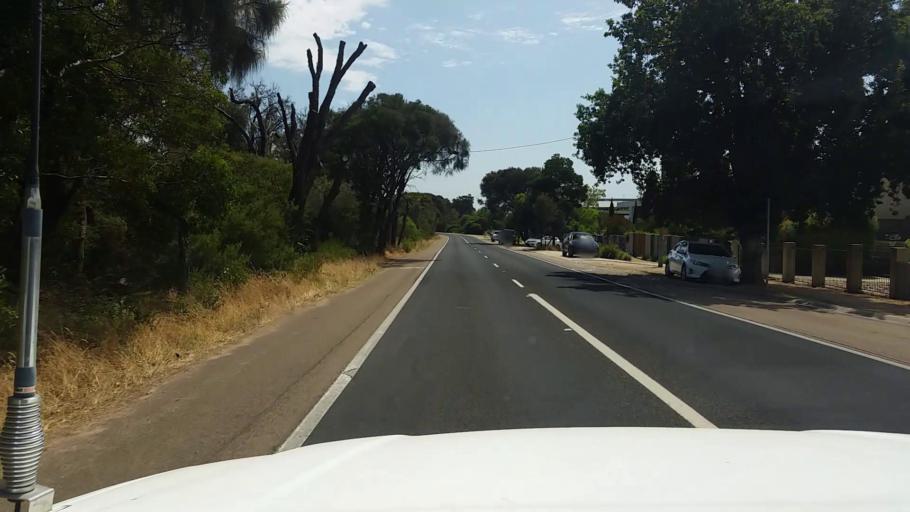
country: AU
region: Victoria
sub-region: Mornington Peninsula
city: Mornington
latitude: -38.2406
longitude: 145.0297
